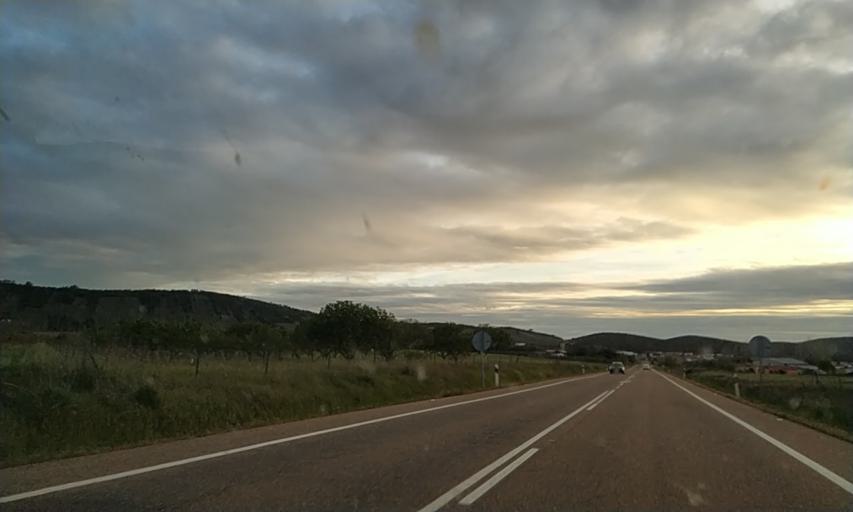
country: ES
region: Extremadura
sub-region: Provincia de Badajoz
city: Puebla de Obando
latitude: 39.1806
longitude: -6.6104
